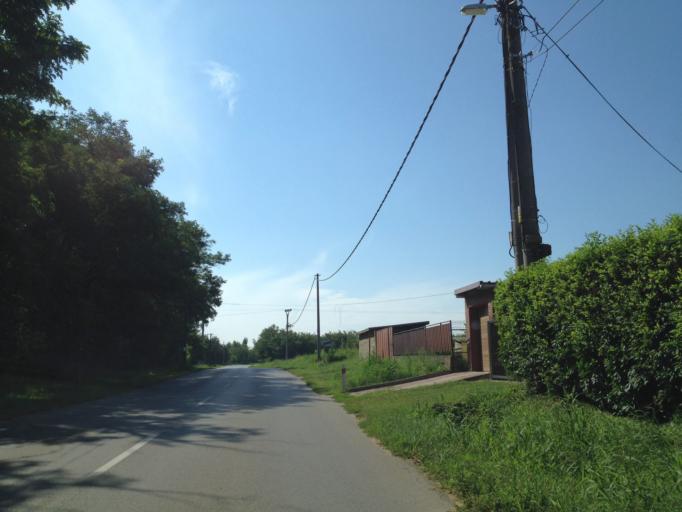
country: SK
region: Nitriansky
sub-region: Okres Komarno
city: Hurbanovo
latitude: 47.8645
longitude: 18.2699
